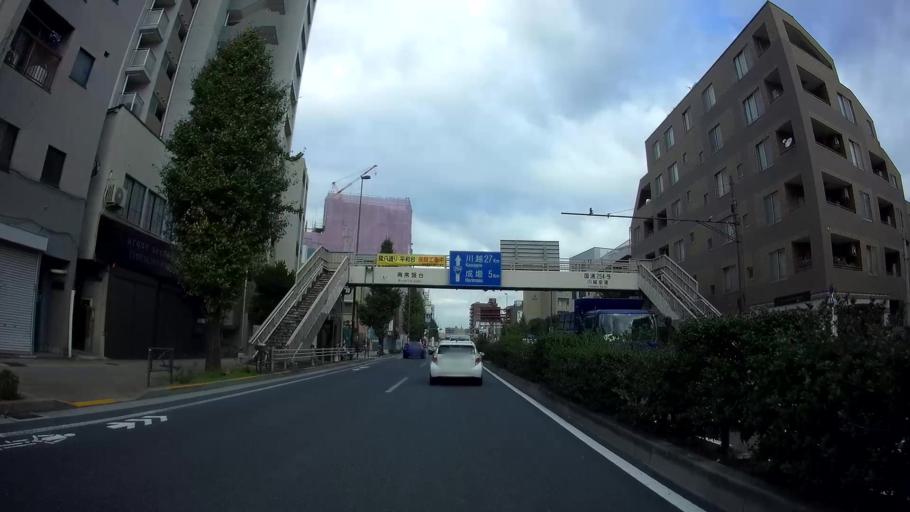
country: JP
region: Saitama
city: Kawaguchi
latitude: 35.7564
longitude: 139.6859
